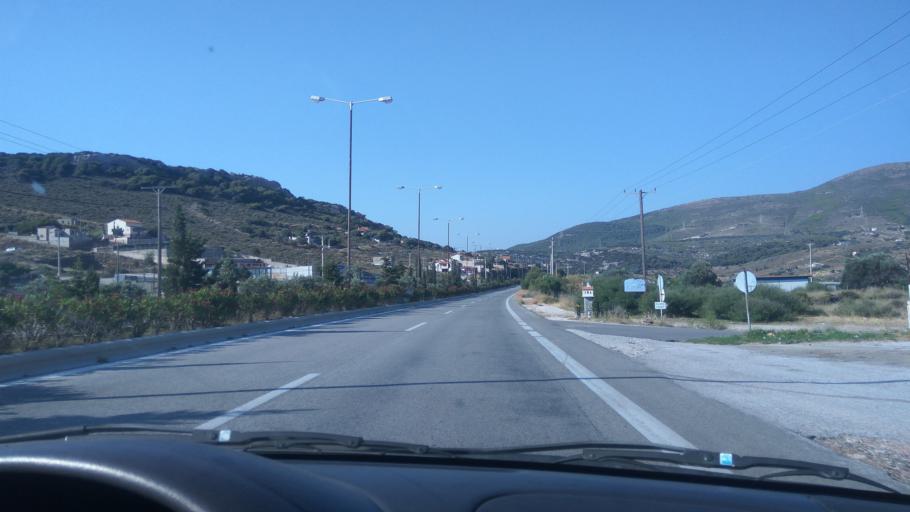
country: GR
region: Attica
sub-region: Nomarchia Anatolikis Attikis
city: Lavrio
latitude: 37.7802
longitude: 24.0570
